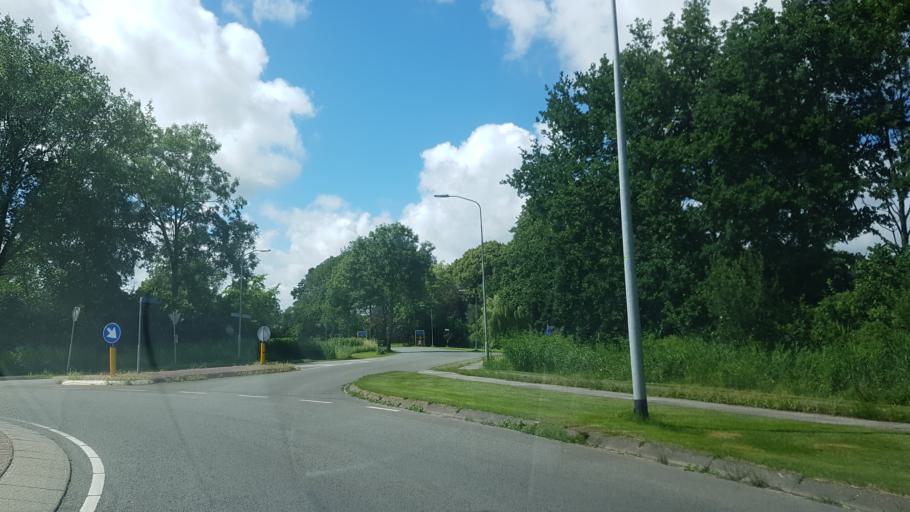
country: NL
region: Groningen
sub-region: Gemeente Bedum
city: Bedum
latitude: 53.4081
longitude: 6.6602
